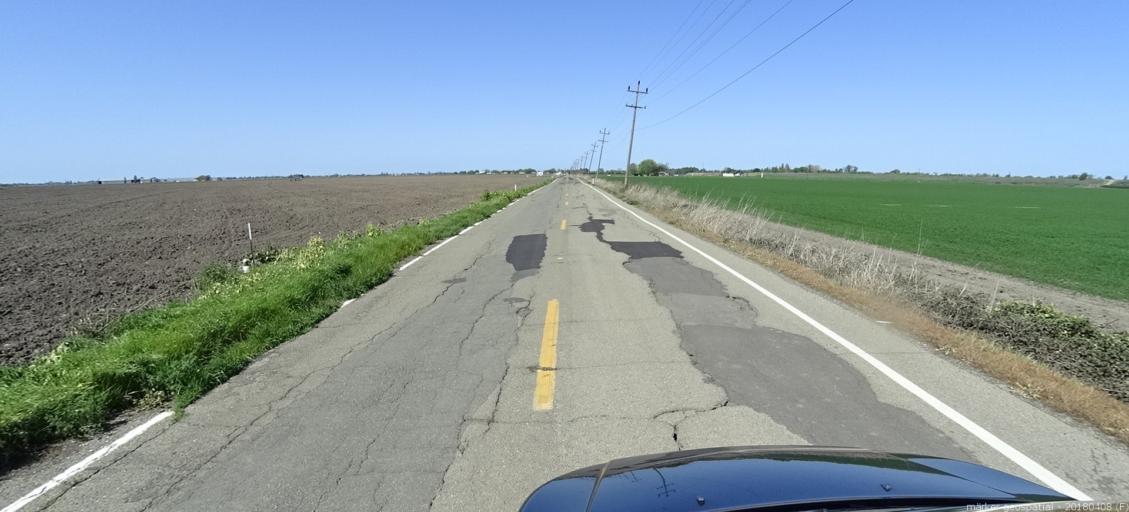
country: US
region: California
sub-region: Sacramento County
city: Walnut Grove
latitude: 38.2877
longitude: -121.5175
